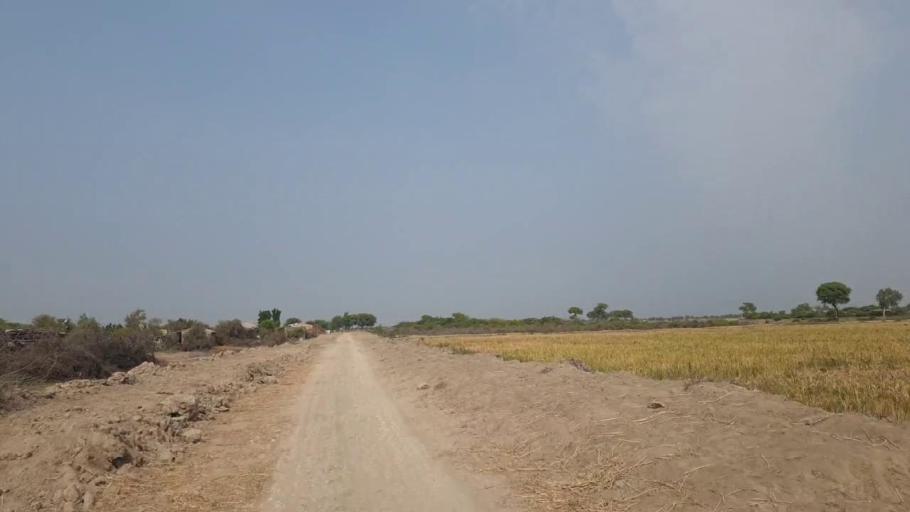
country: PK
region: Sindh
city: Badin
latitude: 24.6160
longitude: 68.7410
